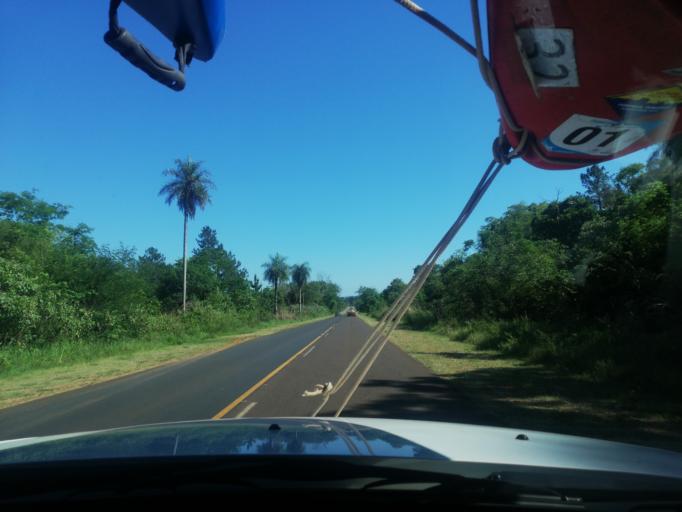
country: AR
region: Misiones
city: Santa Ana
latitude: -27.3489
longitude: -55.5834
